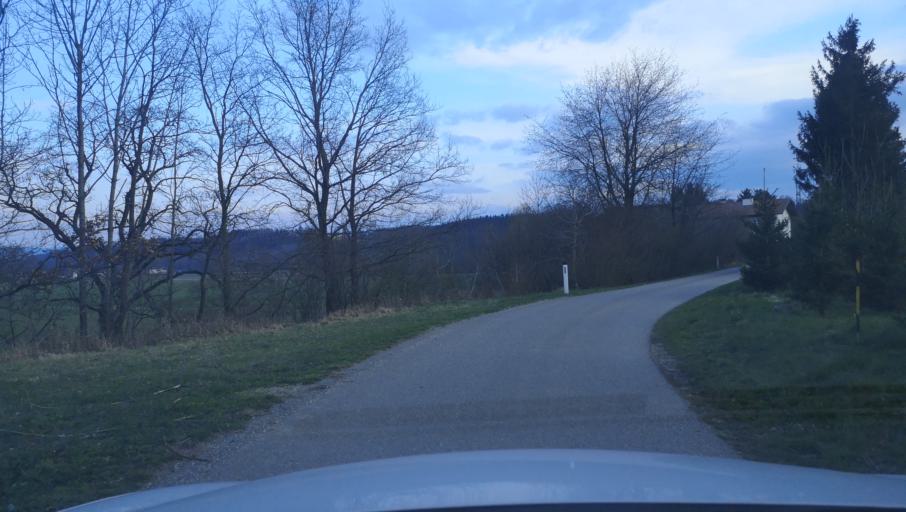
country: AT
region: Lower Austria
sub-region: Politischer Bezirk Amstetten
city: Amstetten
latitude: 48.1080
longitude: 14.8914
